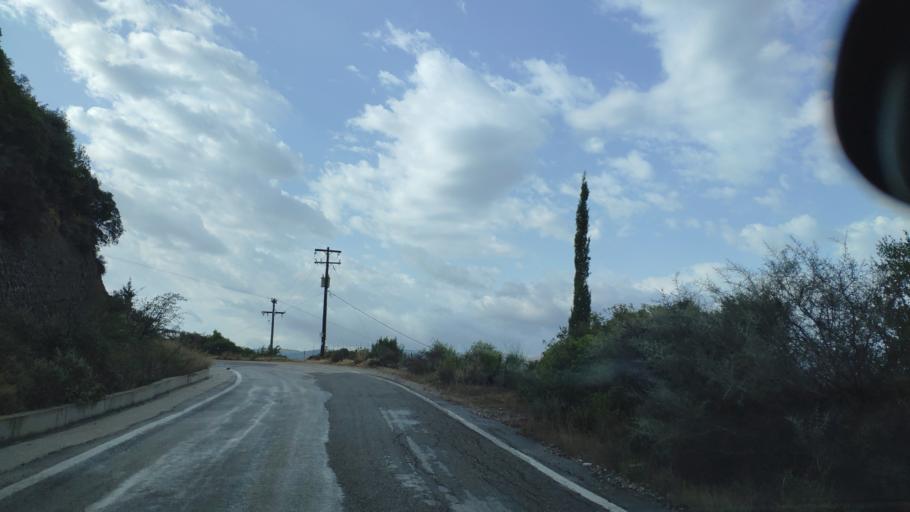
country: GR
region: West Greece
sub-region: Nomos Aitolias kai Akarnanias
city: Sardinia
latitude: 38.8891
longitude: 21.2337
